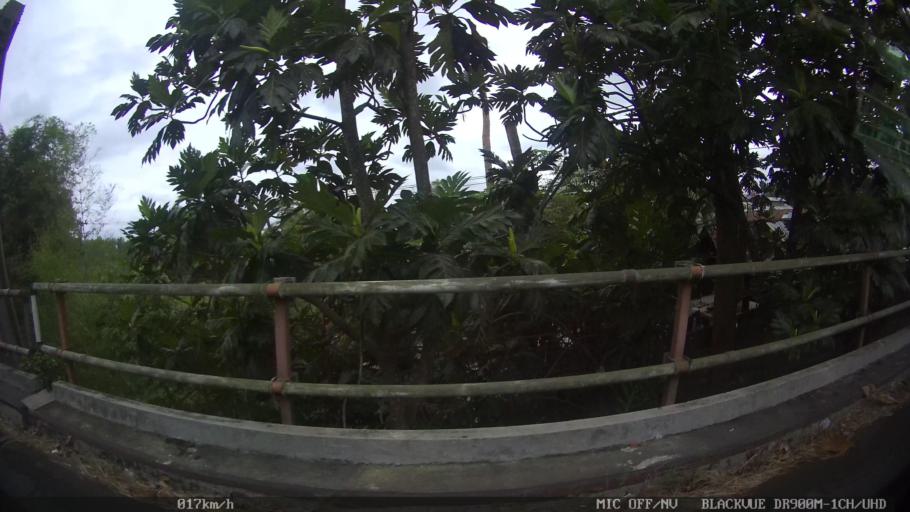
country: ID
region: Daerah Istimewa Yogyakarta
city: Sewon
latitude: -7.8767
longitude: 110.4084
